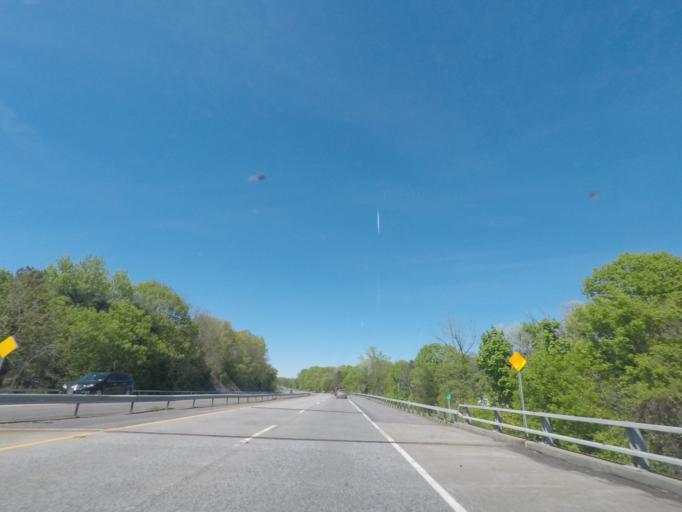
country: US
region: New York
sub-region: Ulster County
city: Kingston
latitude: 41.9367
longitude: -73.9834
